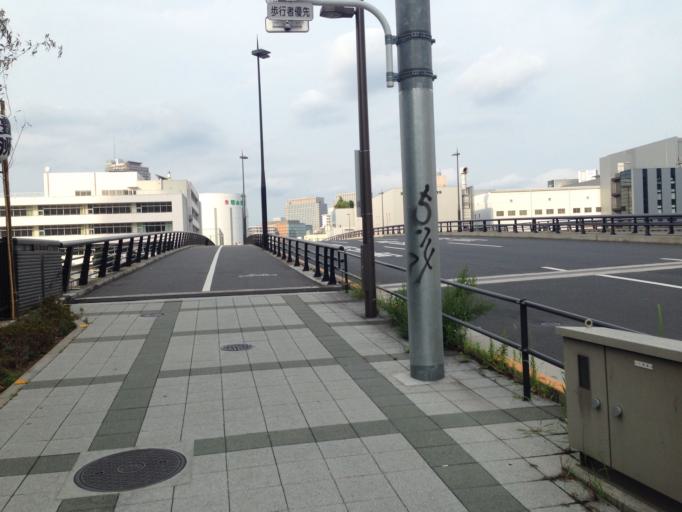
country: JP
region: Tokyo
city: Urayasu
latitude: 35.6617
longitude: 139.7949
